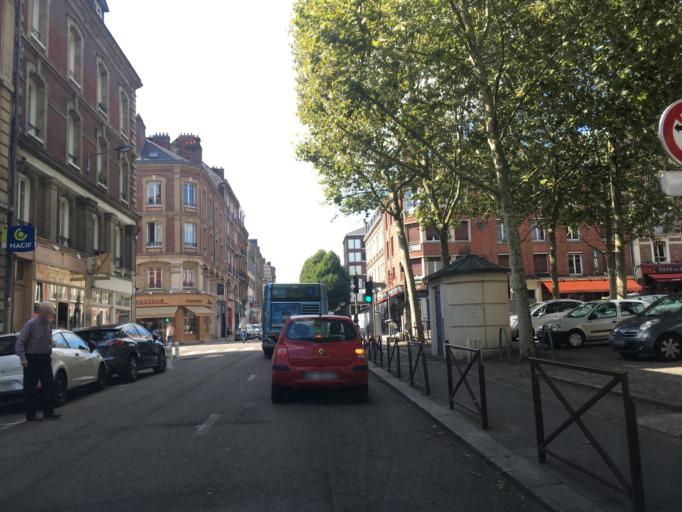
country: FR
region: Haute-Normandie
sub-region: Departement de la Seine-Maritime
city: Rouen
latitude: 49.4402
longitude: 1.1028
